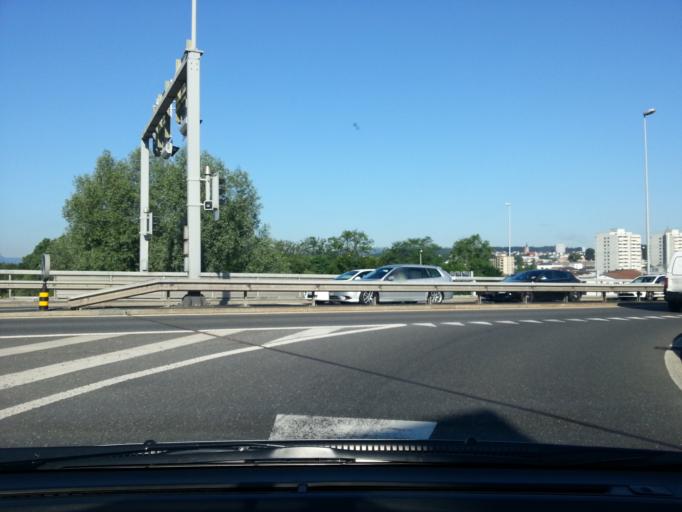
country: CH
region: Lucerne
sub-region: Hochdorf District
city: Emmen
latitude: 47.0713
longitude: 8.2969
